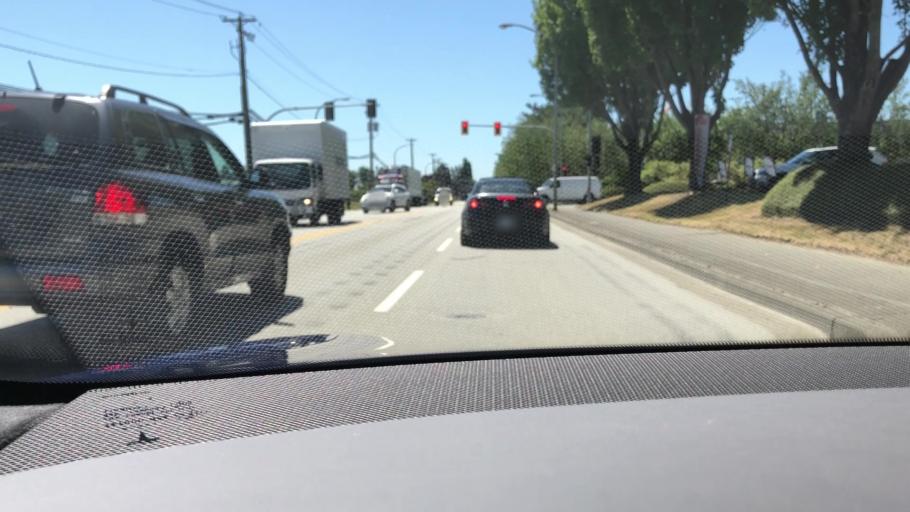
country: CA
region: British Columbia
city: Richmond
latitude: 49.1823
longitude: -123.0692
